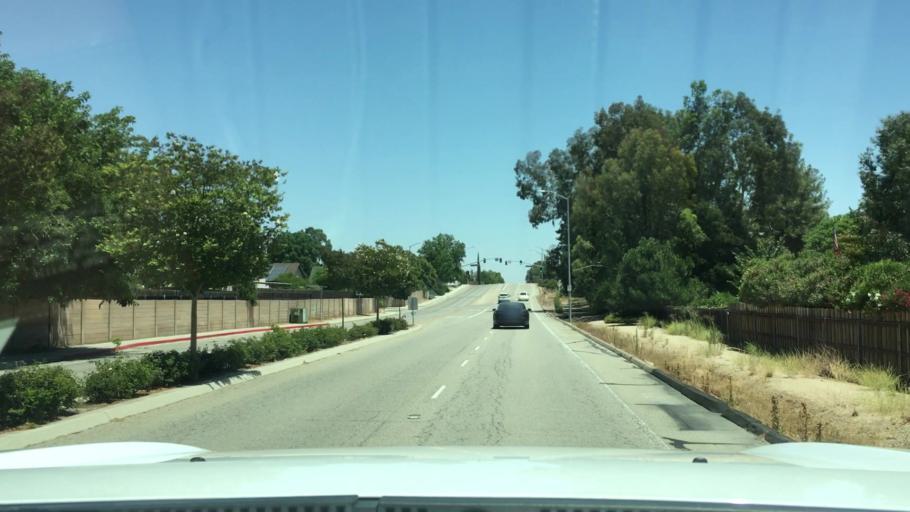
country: US
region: California
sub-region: San Luis Obispo County
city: Paso Robles
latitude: 35.6157
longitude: -120.6676
